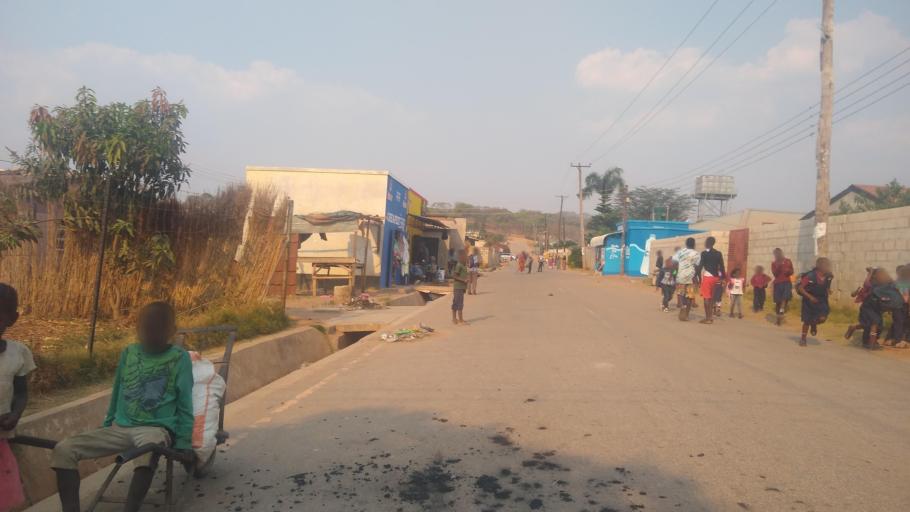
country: ZM
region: Lusaka
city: Lusaka
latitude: -15.4464
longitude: 28.3854
